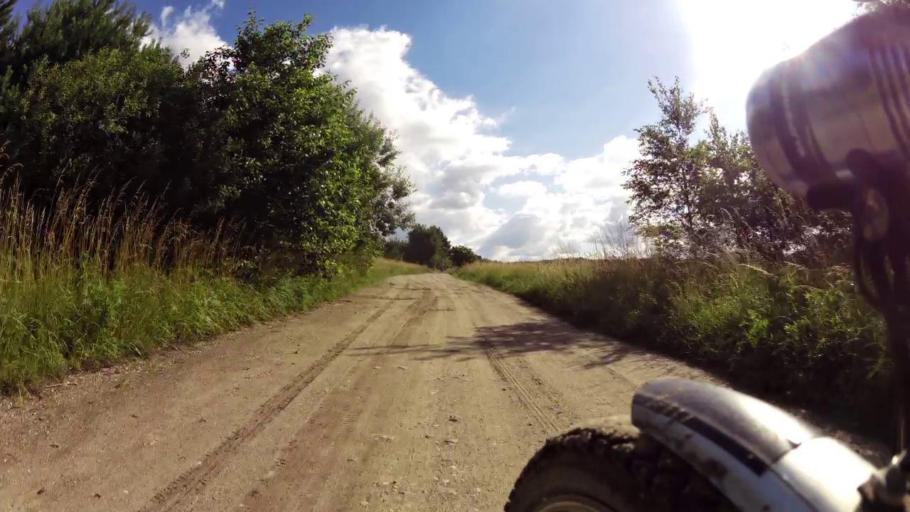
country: PL
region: West Pomeranian Voivodeship
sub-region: Powiat swidwinski
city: Swidwin
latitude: 53.7488
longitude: 15.8935
